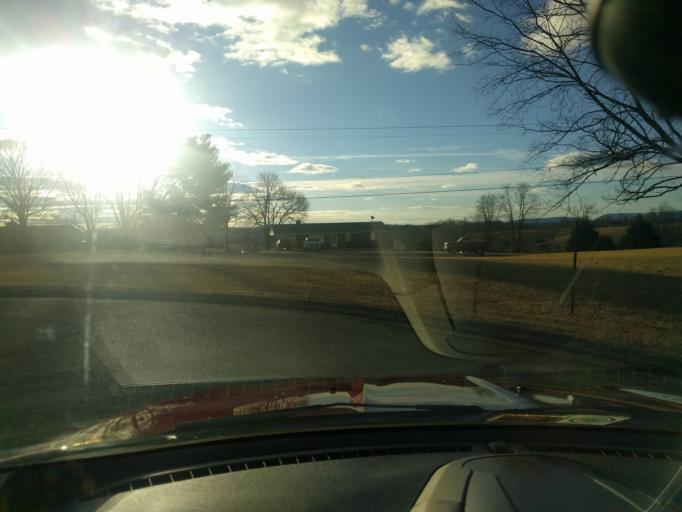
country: US
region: Virginia
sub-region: City of Bedford
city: Bedford
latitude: 37.2254
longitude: -79.5583
